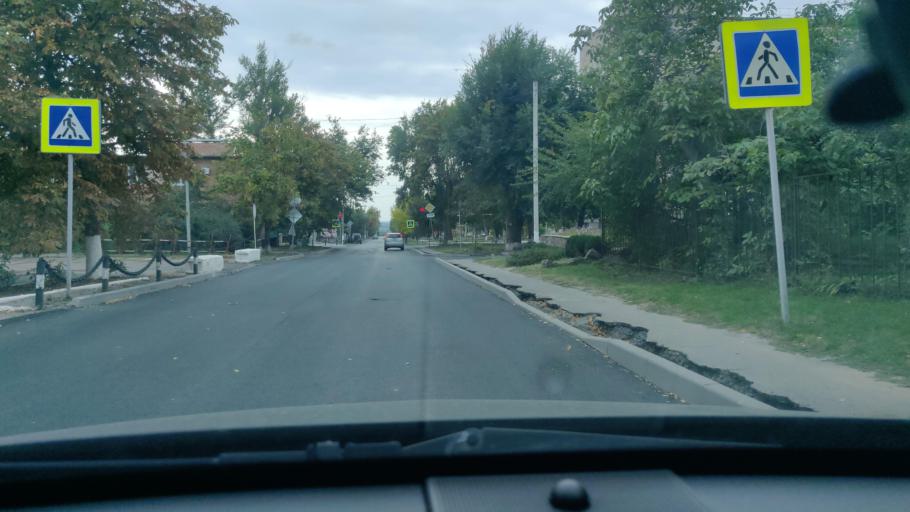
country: RU
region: Rostov
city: Ust'-Donetskiy
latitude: 47.6421
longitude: 40.8733
